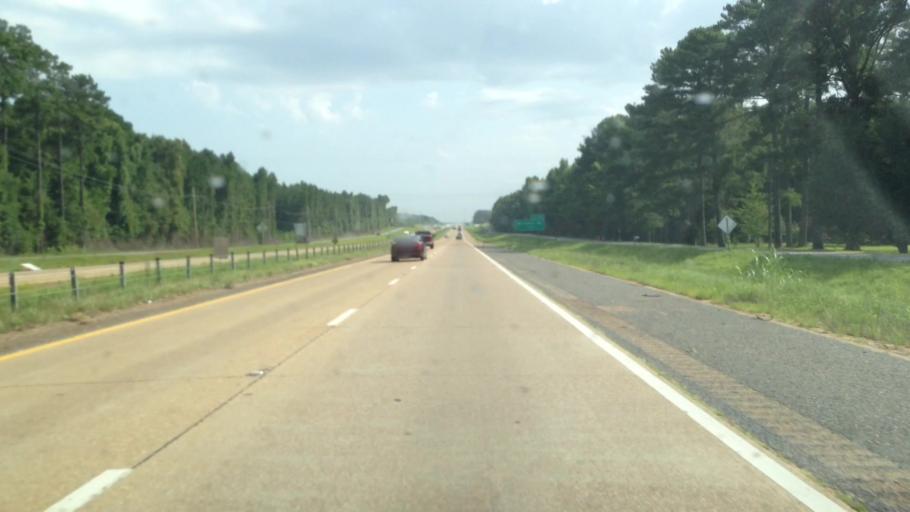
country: US
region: Mississippi
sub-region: Hinds County
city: Terry
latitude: 32.1153
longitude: -90.2954
